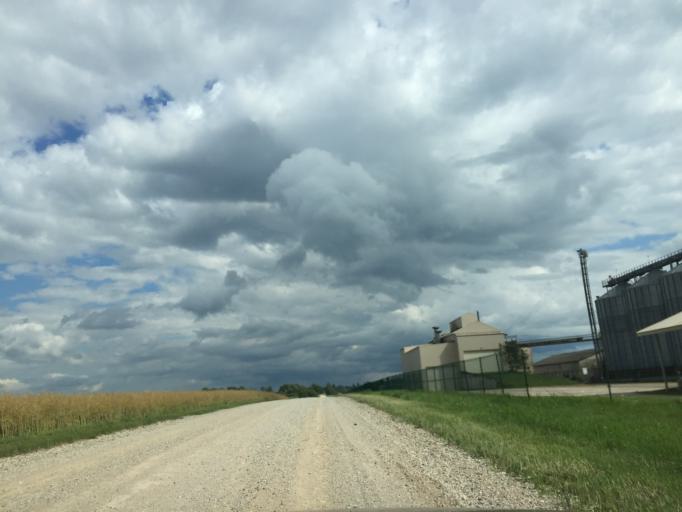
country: LV
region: Malpils
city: Malpils
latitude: 56.8583
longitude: 25.0279
